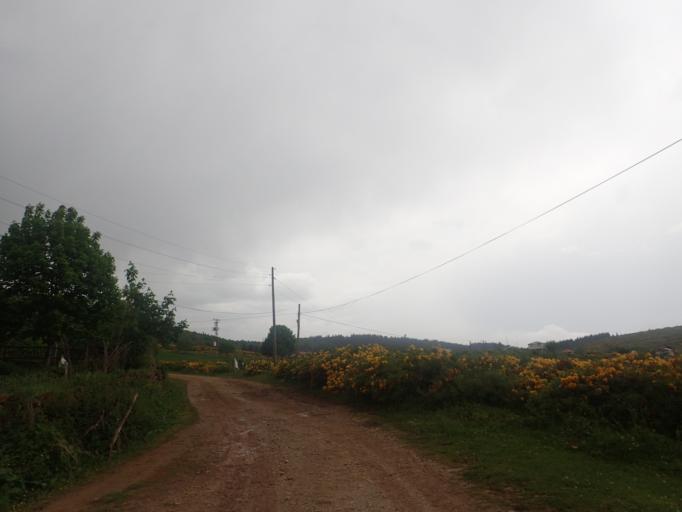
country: TR
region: Ordu
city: Topcam
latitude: 40.6679
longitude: 37.9283
